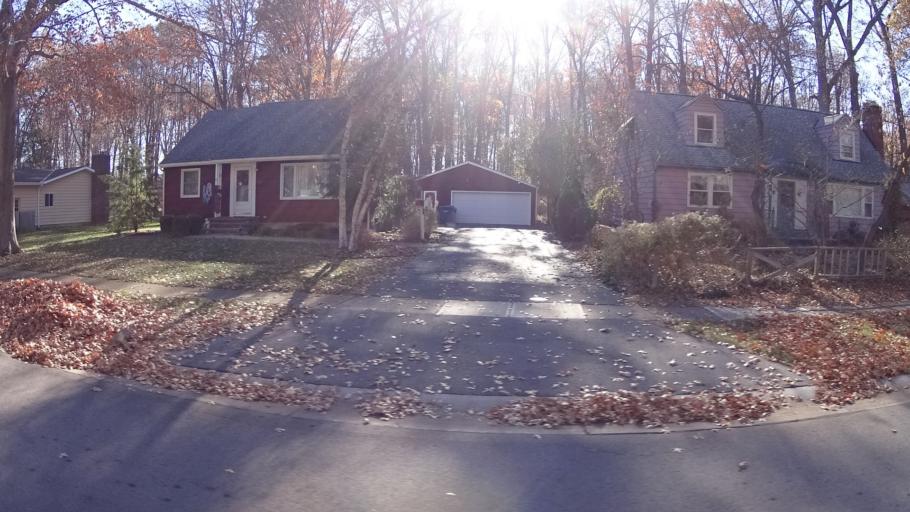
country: US
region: Ohio
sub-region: Lorain County
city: Avon Lake
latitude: 41.5027
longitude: -82.0360
